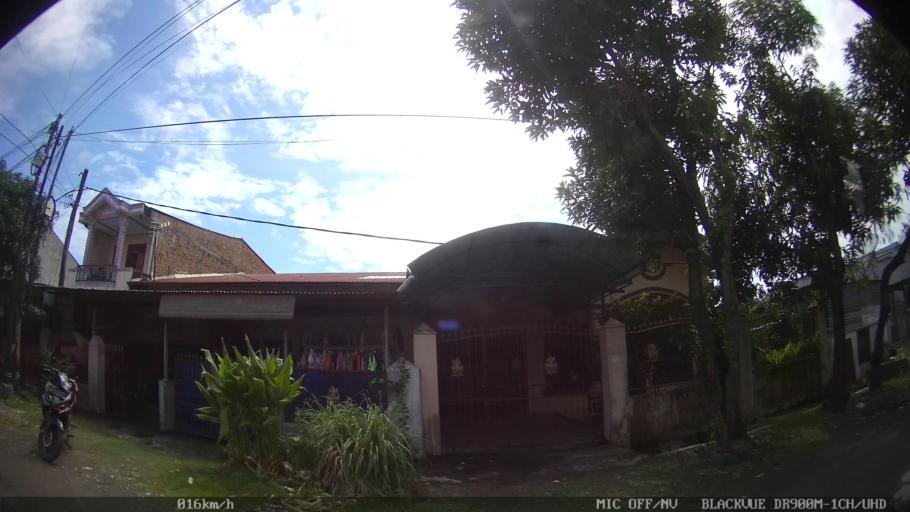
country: ID
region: North Sumatra
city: Medan
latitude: 3.5896
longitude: 98.7345
